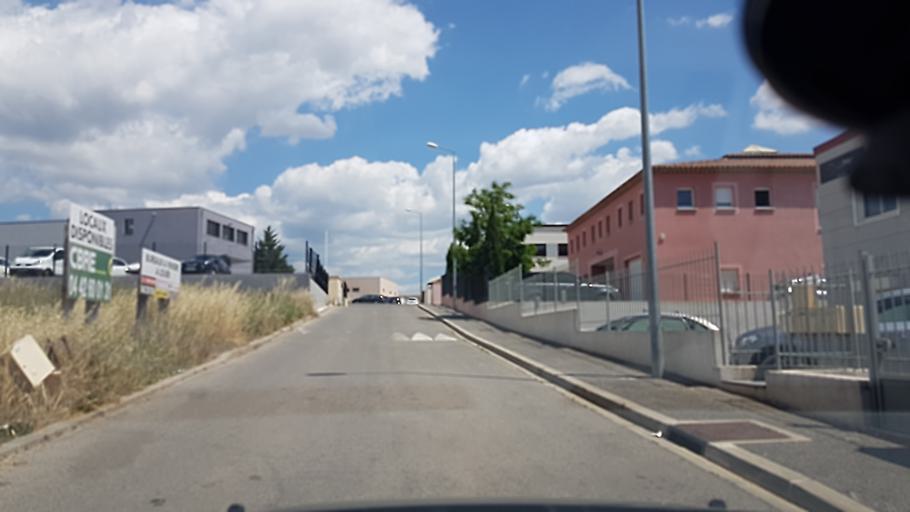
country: FR
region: Provence-Alpes-Cote d'Azur
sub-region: Departement des Bouches-du-Rhone
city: Eguilles
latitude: 43.5474
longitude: 5.3617
